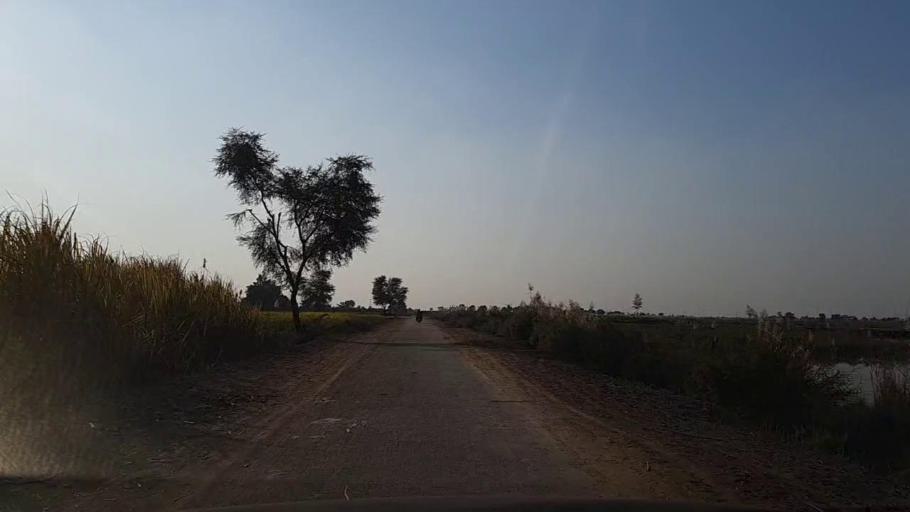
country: PK
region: Sindh
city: Daur
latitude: 26.3718
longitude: 68.2773
